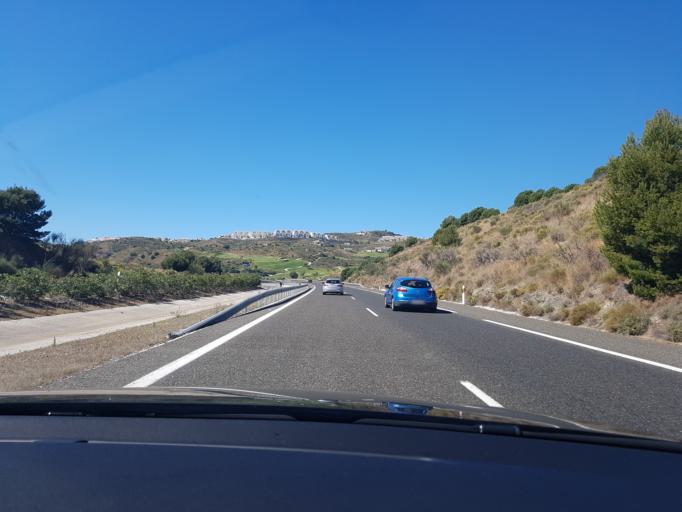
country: ES
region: Andalusia
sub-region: Provincia de Malaga
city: Fuengirola
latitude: 36.5153
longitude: -4.6979
